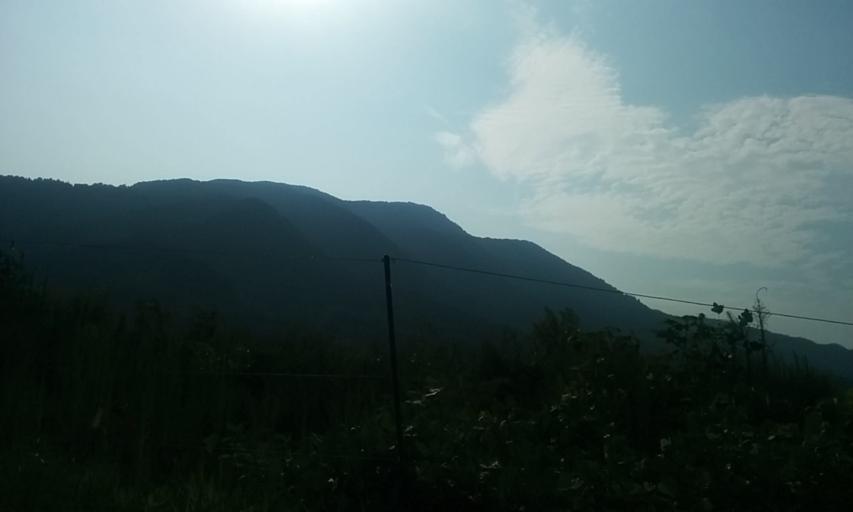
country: JP
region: Kyoto
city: Maizuru
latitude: 35.4995
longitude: 135.2924
